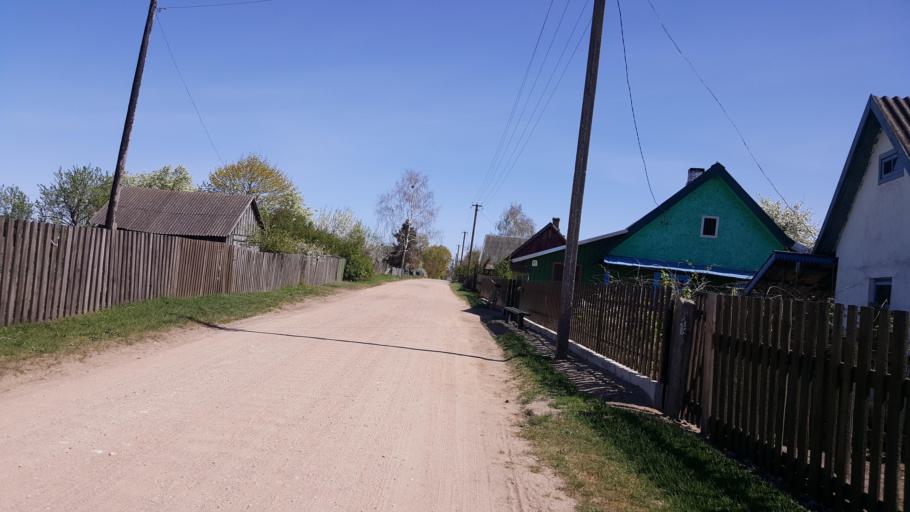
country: BY
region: Brest
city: Kamyanyets
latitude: 52.4557
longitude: 23.8788
